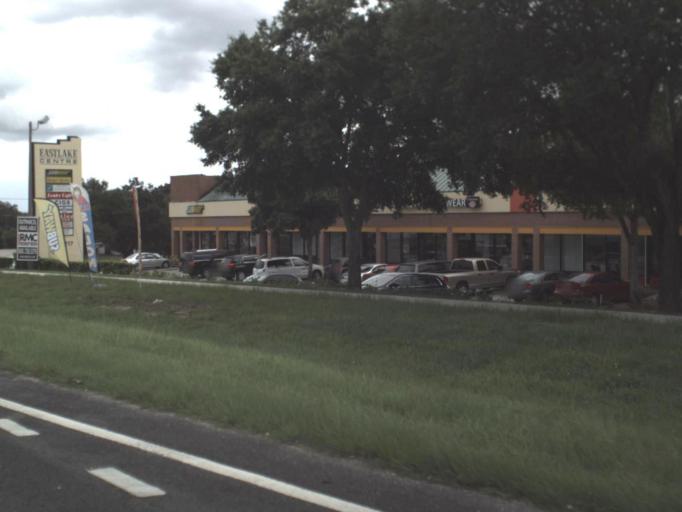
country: US
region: Florida
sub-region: Hillsborough County
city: East Lake-Orient Park
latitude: 27.9961
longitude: -82.3869
